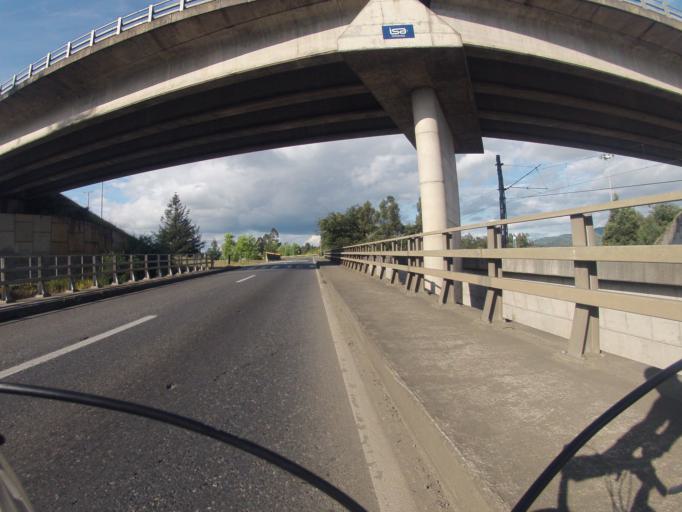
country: CL
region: Araucania
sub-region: Provincia de Cautin
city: Temuco
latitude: -38.7855
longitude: -72.6128
